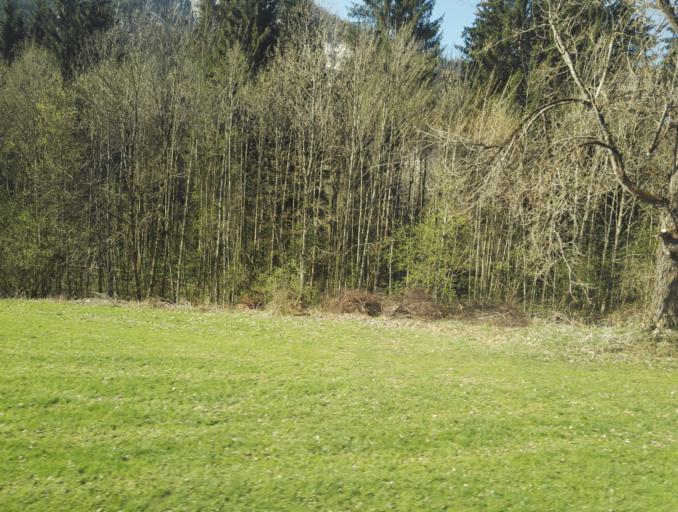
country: AT
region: Salzburg
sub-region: Politischer Bezirk Sankt Johann im Pongau
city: Forstau
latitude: 47.4024
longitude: 13.5782
